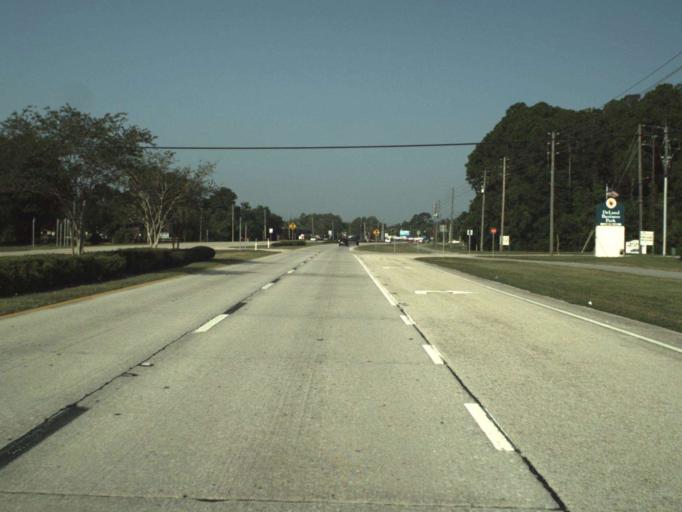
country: US
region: Florida
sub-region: Volusia County
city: North DeLand
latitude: 29.0575
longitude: -81.2760
